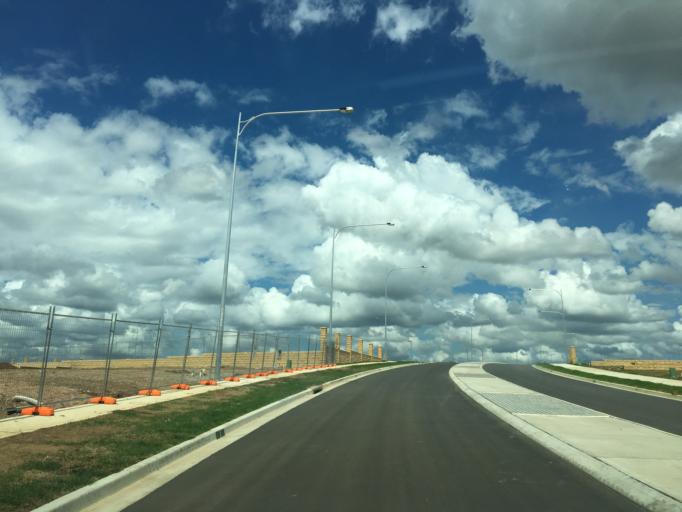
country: AU
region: New South Wales
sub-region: Campbelltown Municipality
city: Denham Court
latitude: -33.9878
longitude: 150.7979
